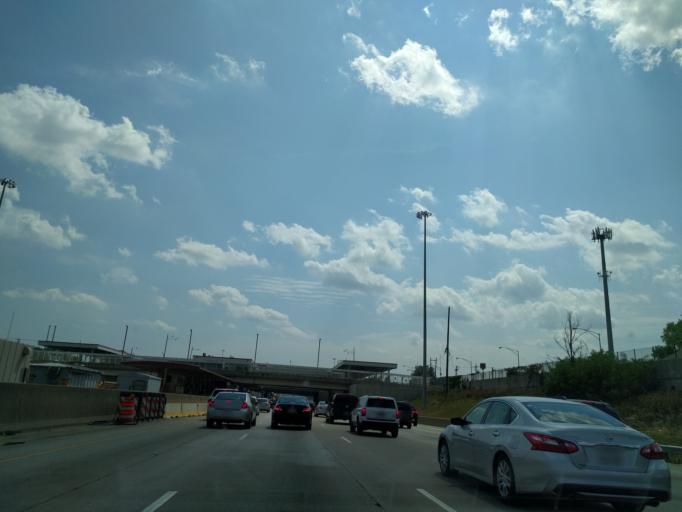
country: US
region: Illinois
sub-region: Cook County
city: Calumet Park
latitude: 41.7239
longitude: -87.6246
